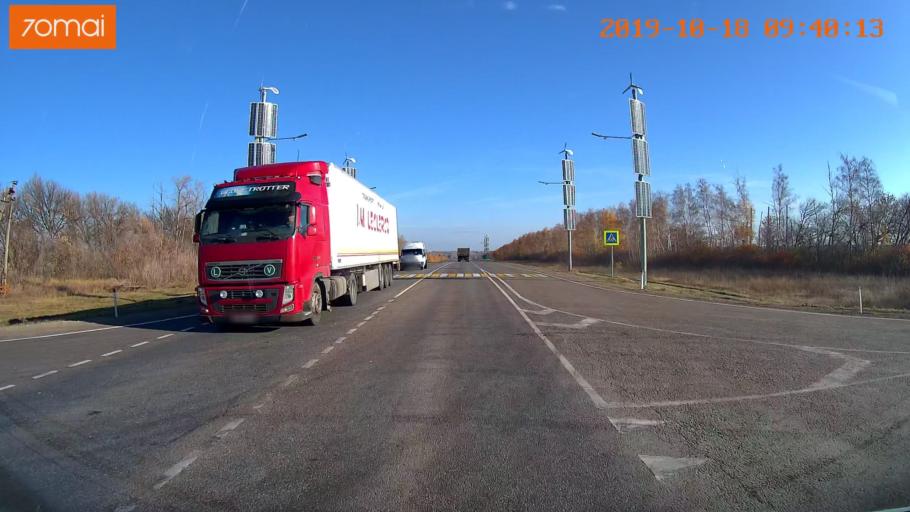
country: RU
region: Tula
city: Yefremov
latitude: 53.2615
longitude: 38.1451
